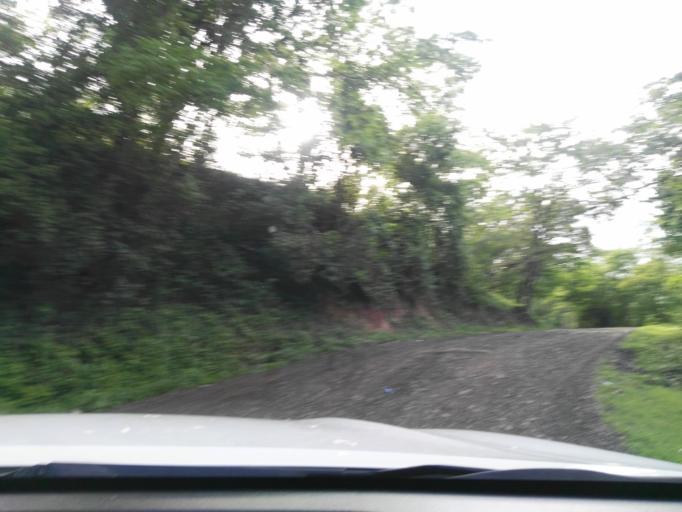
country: NI
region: Matagalpa
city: Terrabona
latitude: 12.8451
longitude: -86.0377
